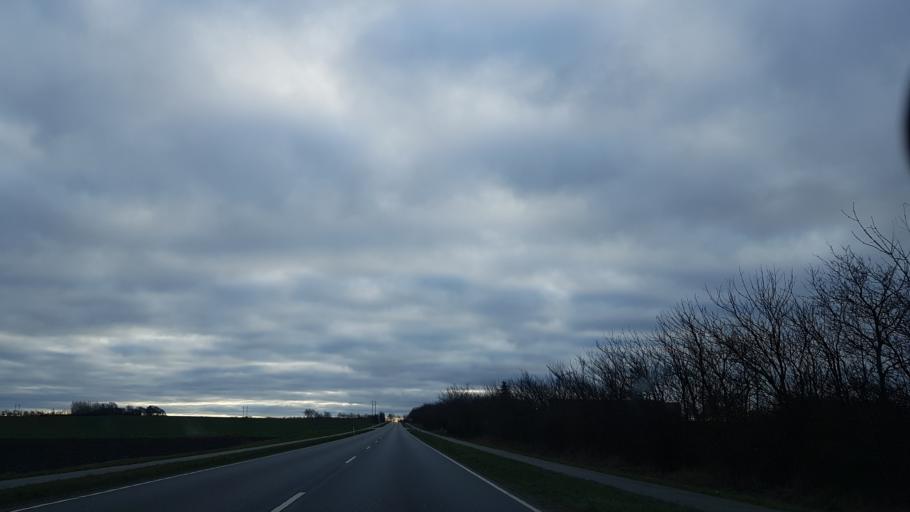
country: DK
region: Zealand
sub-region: Kalundborg Kommune
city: Gorlev
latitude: 55.5757
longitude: 11.1924
